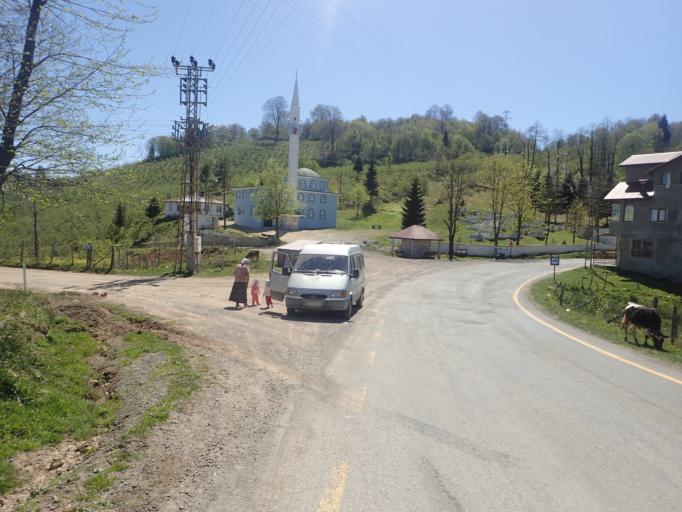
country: TR
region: Ordu
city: Kabaduz
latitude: 40.7973
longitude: 37.9155
